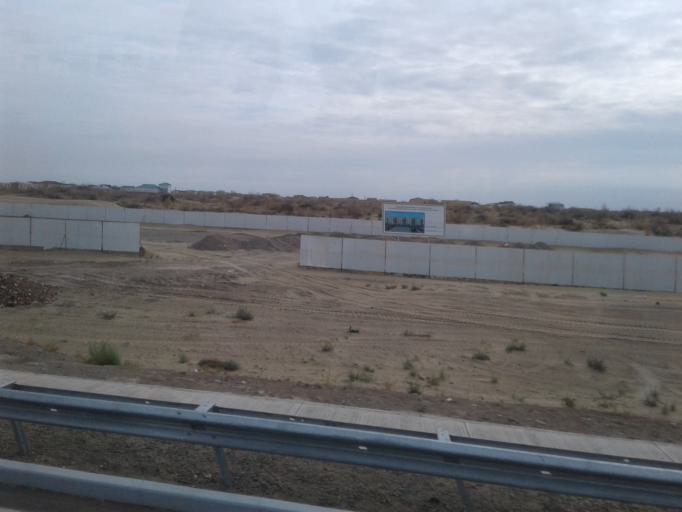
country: TM
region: Lebap
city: Turkmenabat
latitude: 38.9749
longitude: 63.5479
